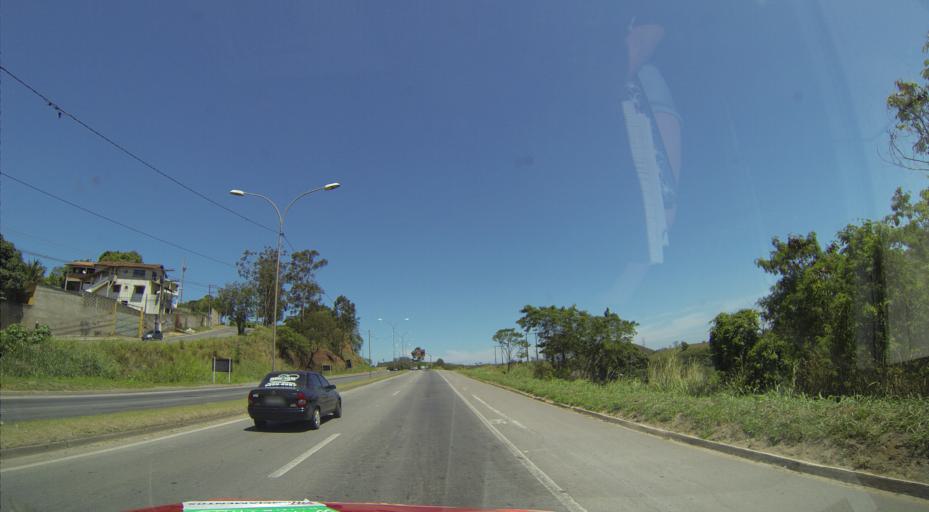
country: BR
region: Espirito Santo
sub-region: Serra
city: Serra
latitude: -20.1619
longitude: -40.2753
